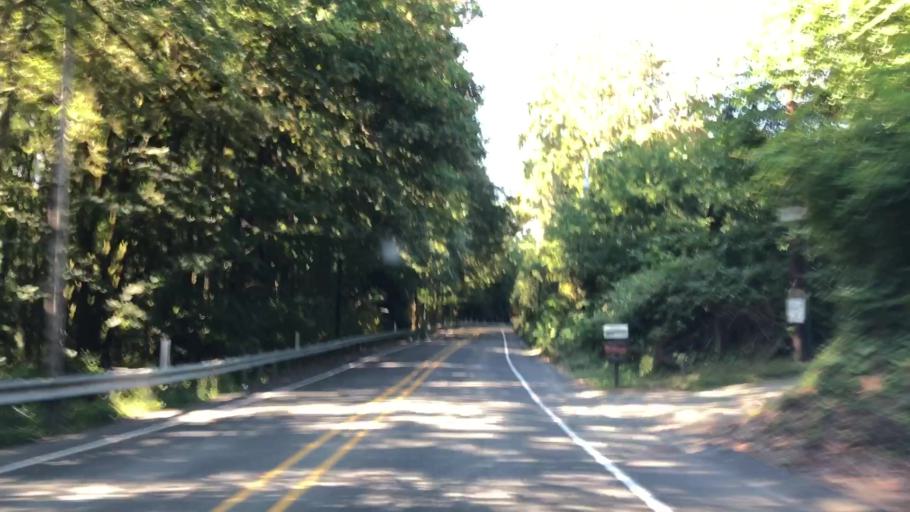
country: US
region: Washington
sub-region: Kitsap County
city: Kingston
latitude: 47.7792
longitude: -122.4996
